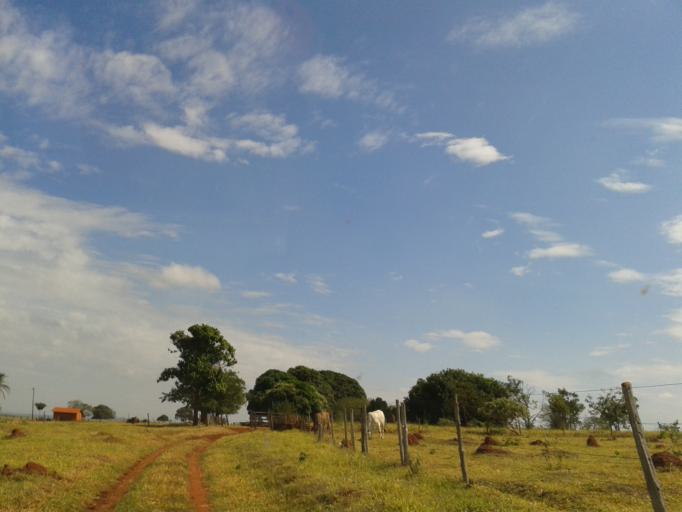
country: BR
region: Minas Gerais
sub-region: Campina Verde
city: Campina Verde
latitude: -19.3774
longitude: -49.6720
